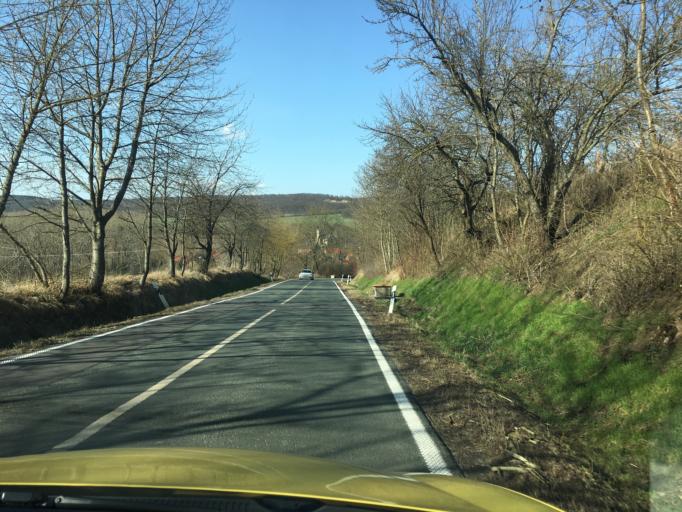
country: DE
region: Thuringia
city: Ostramondra
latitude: 51.1930
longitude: 11.3569
